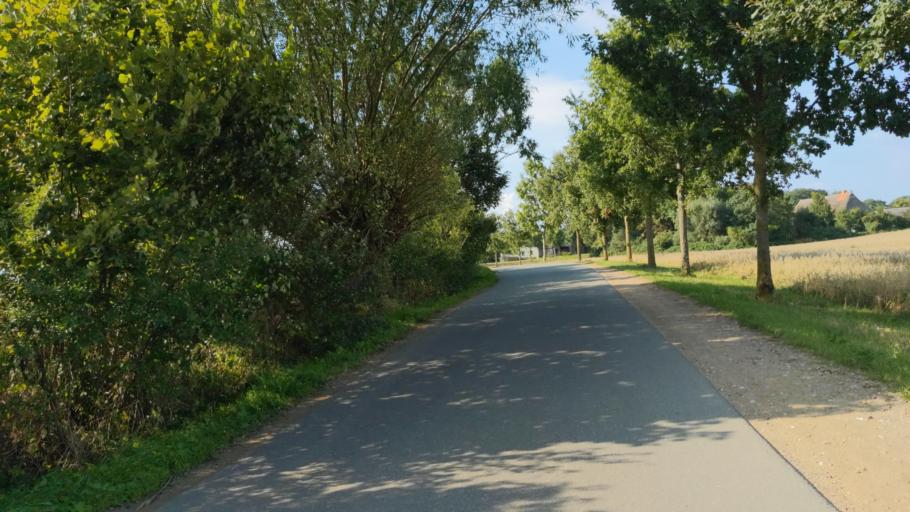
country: DE
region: Mecklenburg-Vorpommern
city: Kalkhorst
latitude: 53.9631
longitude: 11.0102
